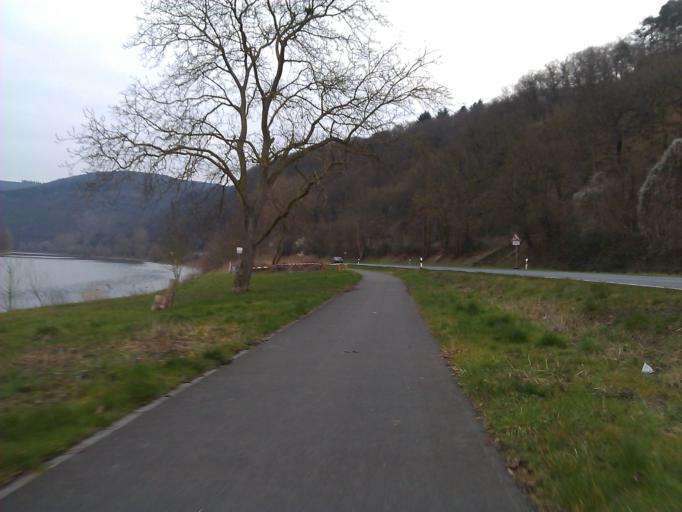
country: DE
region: Rheinland-Pfalz
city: Osterspai
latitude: 50.2432
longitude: 7.6272
